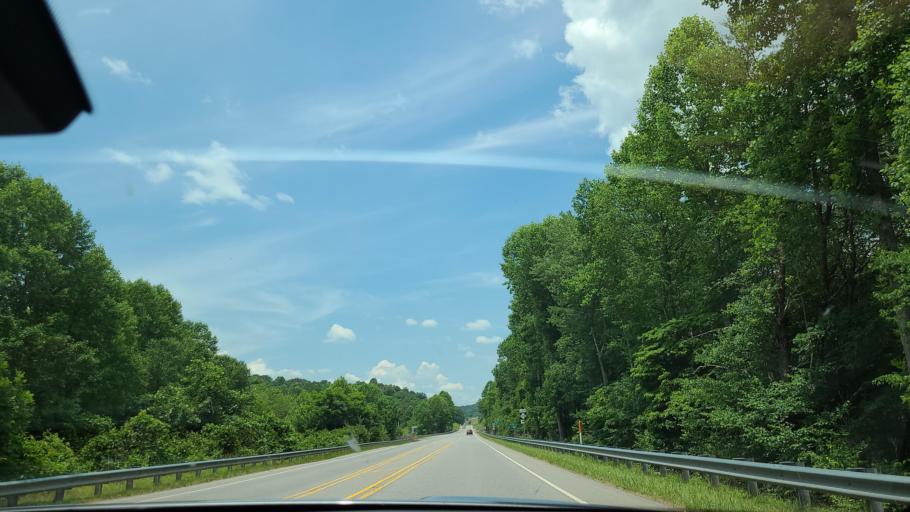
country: US
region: North Carolina
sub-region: Clay County
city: Hayesville
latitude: 35.0338
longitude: -83.7385
